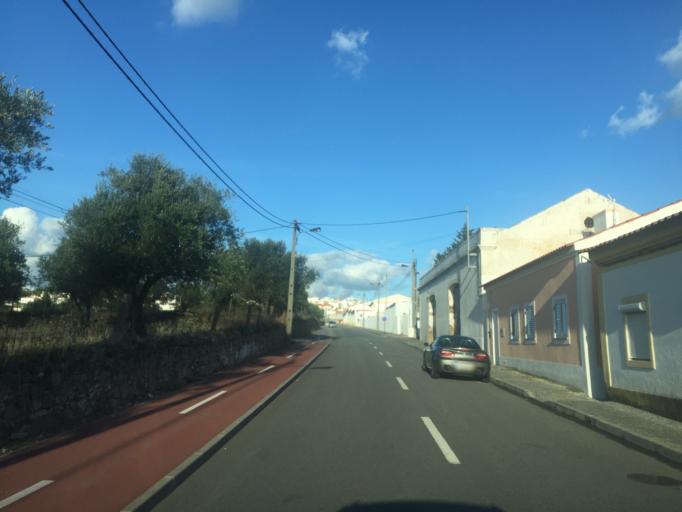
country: PT
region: Portalegre
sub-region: Alter do Chao
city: Alter do Chao
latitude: 39.1983
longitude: -7.6651
